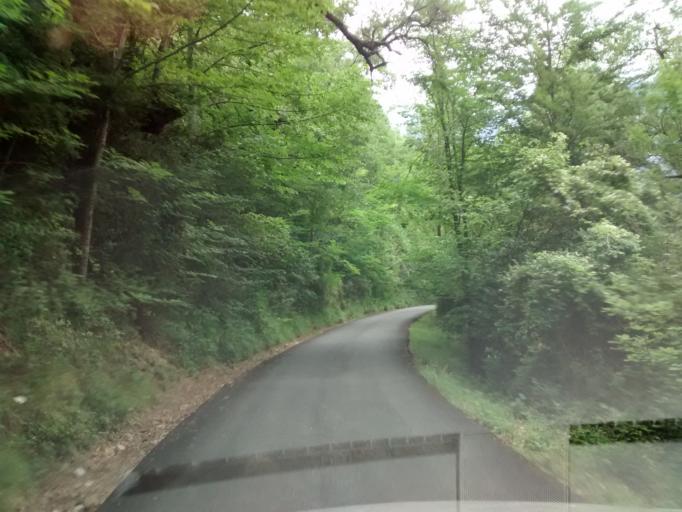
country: ES
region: Aragon
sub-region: Provincia de Huesca
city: Puertolas
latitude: 42.5878
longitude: 0.1344
